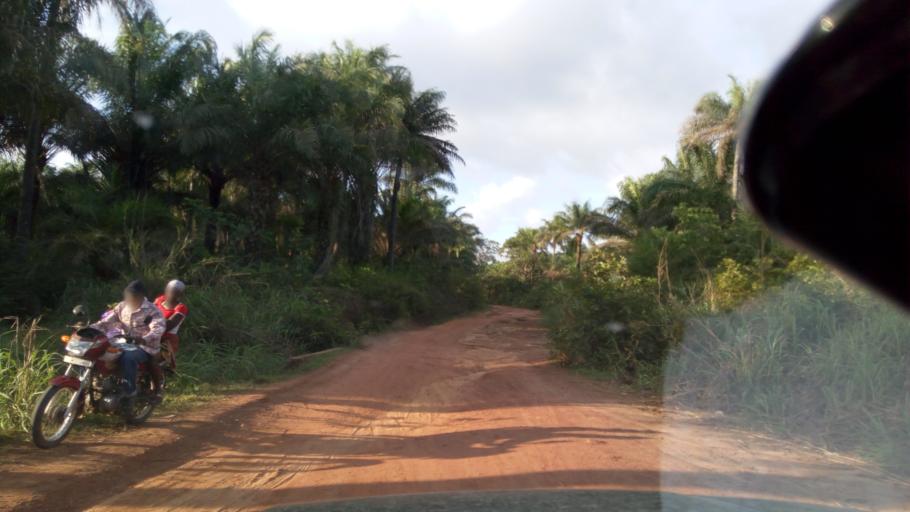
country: SL
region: Northern Province
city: Konakridee
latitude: 8.7577
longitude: -13.1412
